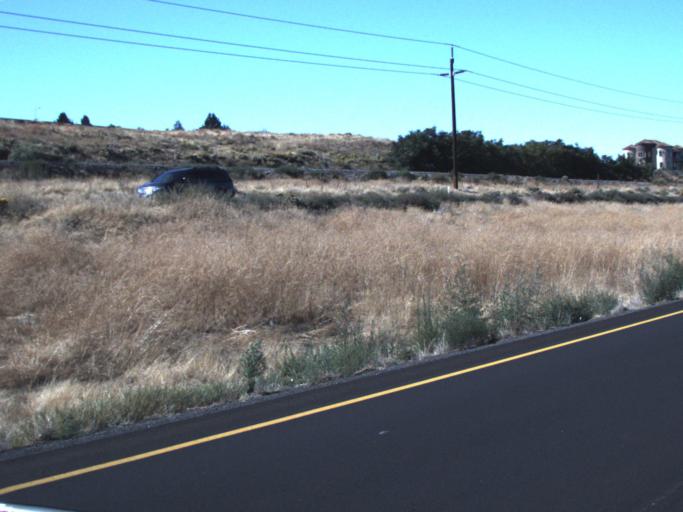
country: US
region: Washington
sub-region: Benton County
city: Kennewick
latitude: 46.2215
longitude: -119.1569
